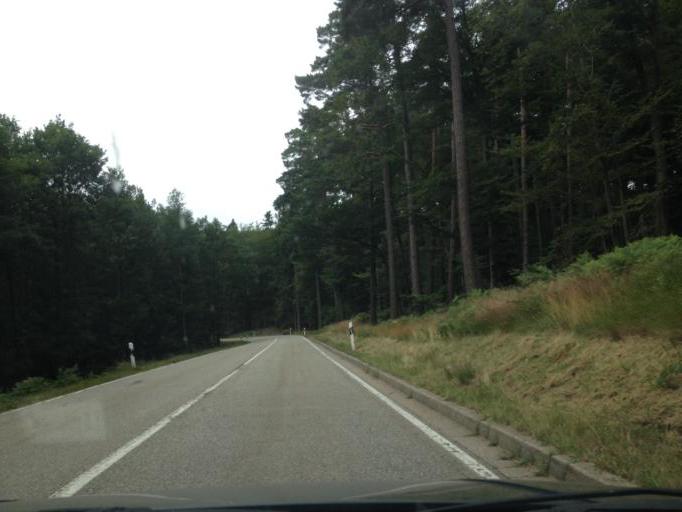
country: DE
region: Rheinland-Pfalz
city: Waldleiningen
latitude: 49.3140
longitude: 7.8603
